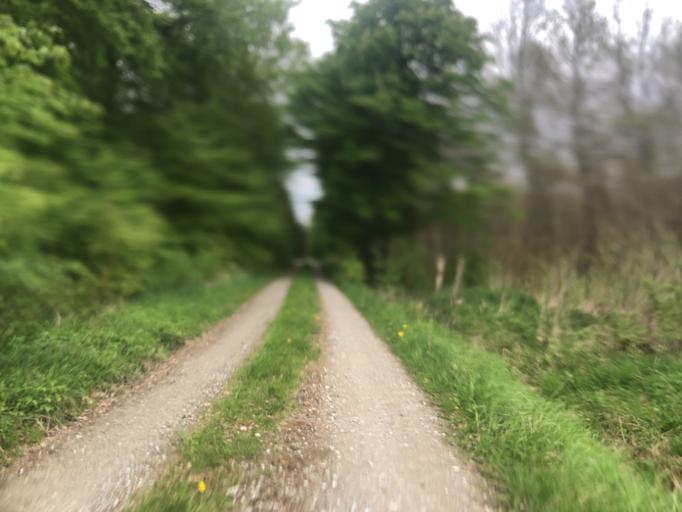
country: DK
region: Zealand
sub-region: Koge Kommune
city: Ejby
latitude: 55.4421
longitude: 12.0920
